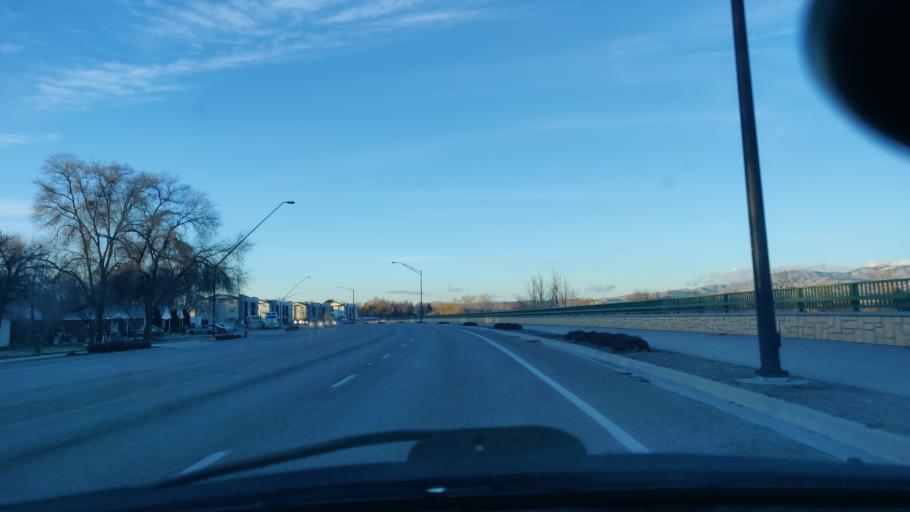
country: US
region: Idaho
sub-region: Ada County
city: Boise
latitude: 43.5809
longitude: -116.1986
